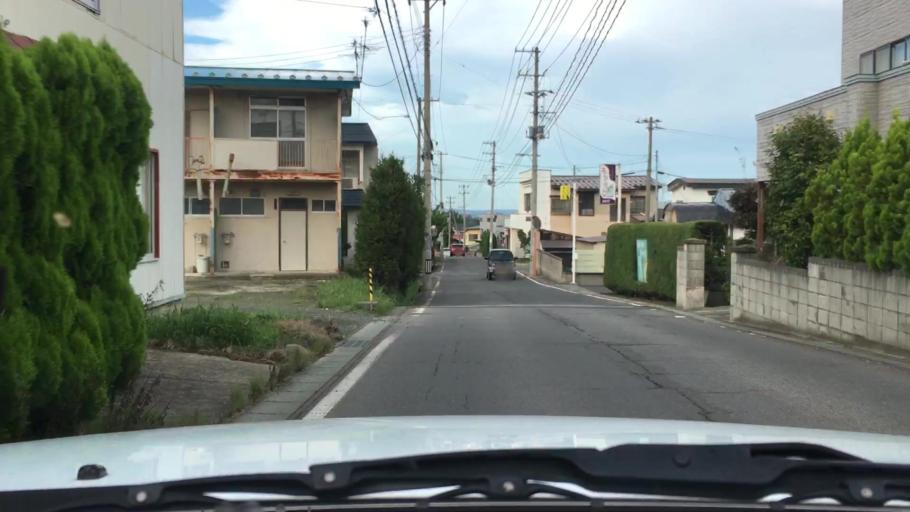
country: JP
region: Aomori
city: Hirosaki
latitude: 40.5807
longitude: 140.4581
